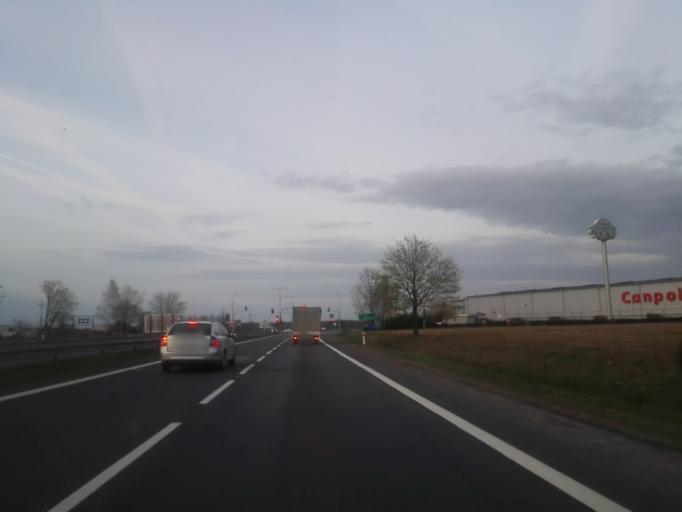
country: PL
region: Masovian Voivodeship
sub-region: Powiat zyrardowski
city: Radziejowice
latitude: 52.0086
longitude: 20.6069
